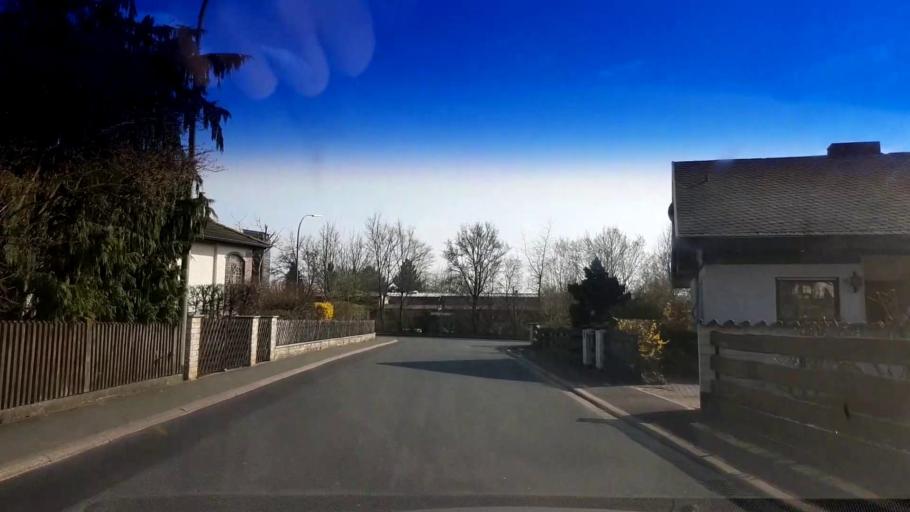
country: DE
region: Bavaria
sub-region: Upper Franconia
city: Oberhaid
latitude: 49.9368
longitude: 10.8098
